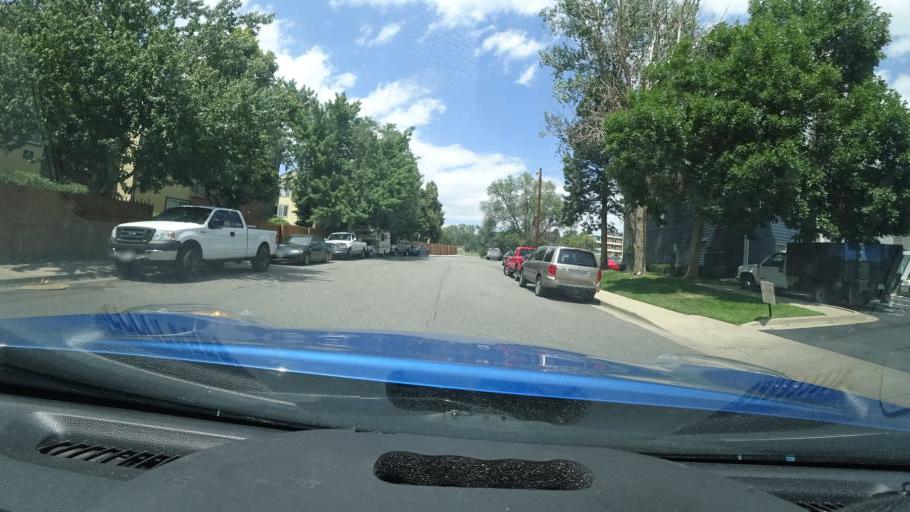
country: US
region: Colorado
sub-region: Arapahoe County
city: Sheridan
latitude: 39.6584
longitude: -105.0298
